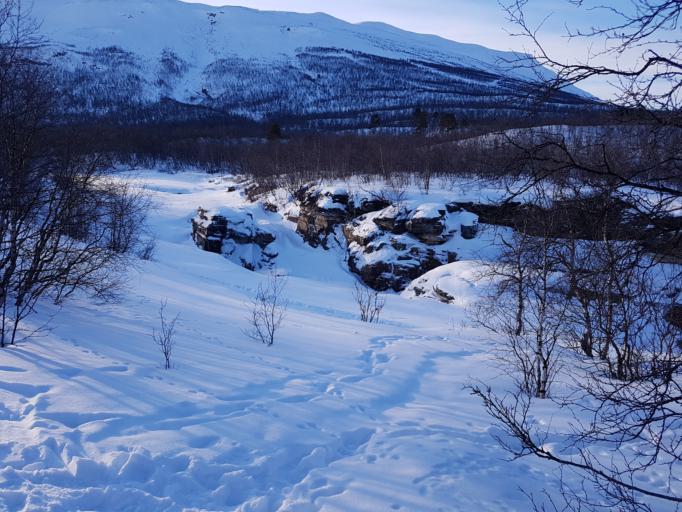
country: NO
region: Troms
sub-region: Bardu
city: Setermoen
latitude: 68.3558
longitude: 18.7709
